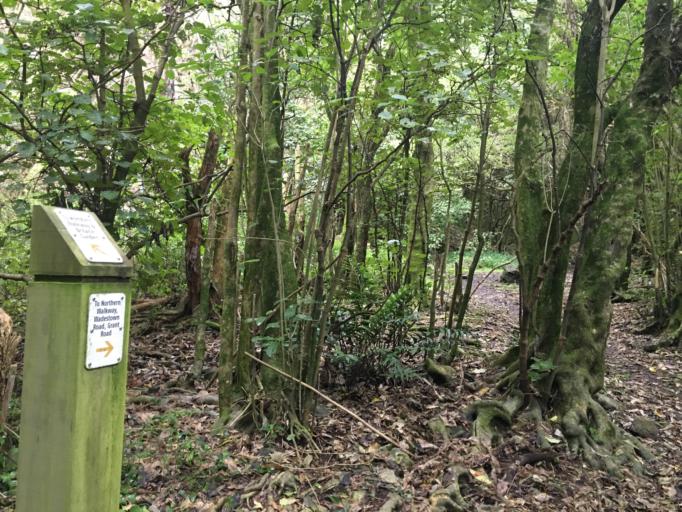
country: NZ
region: Wellington
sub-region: Wellington City
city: Kelburn
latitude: -41.2729
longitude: 174.7701
